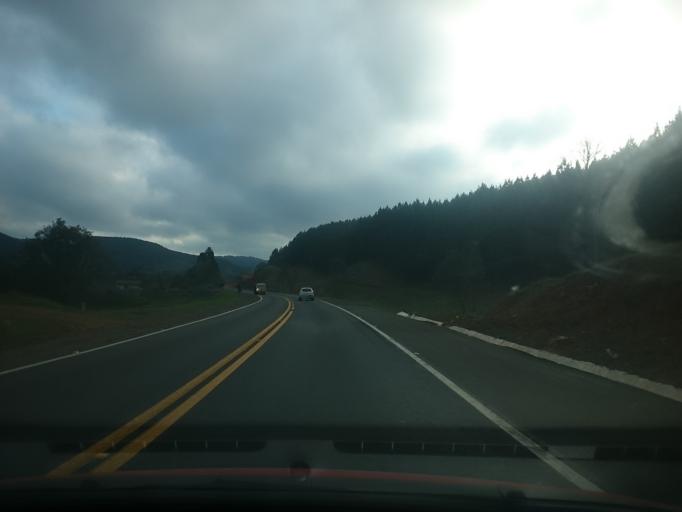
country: BR
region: Santa Catarina
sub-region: Lages
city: Lages
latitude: -27.9450
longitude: -50.4740
